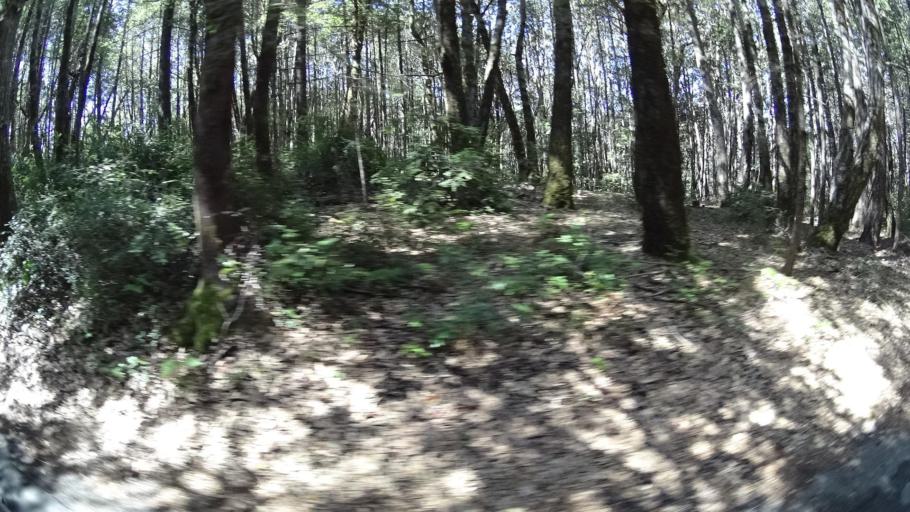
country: US
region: California
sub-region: Humboldt County
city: Rio Dell
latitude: 40.2091
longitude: -124.1054
